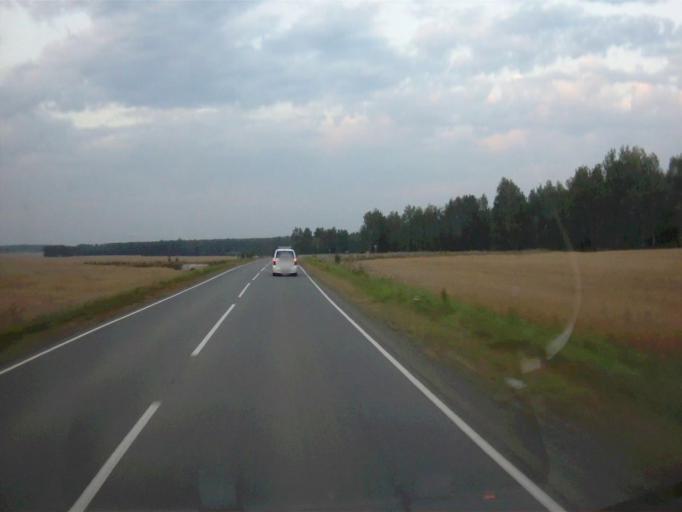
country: RU
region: Chelyabinsk
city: Chebarkul'
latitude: 55.1732
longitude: 60.4530
